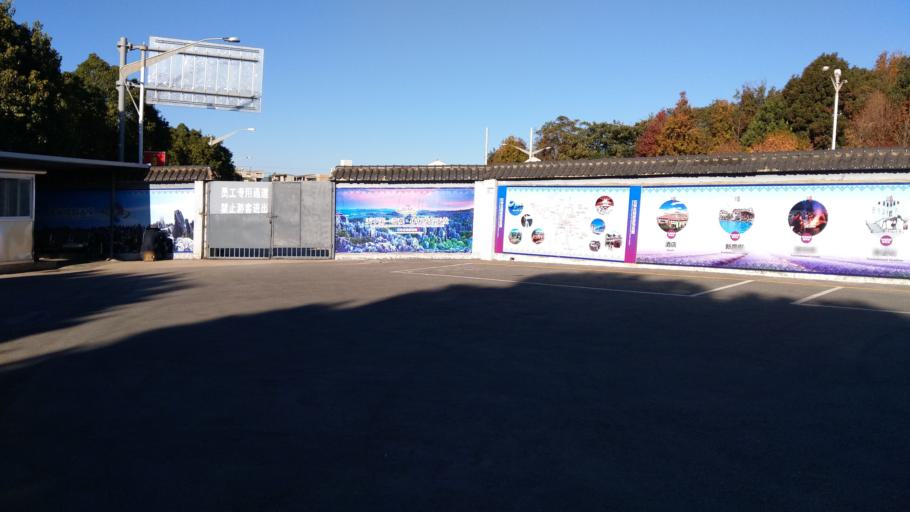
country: CN
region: Yunnan
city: Shilin
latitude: 24.8268
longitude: 103.3229
